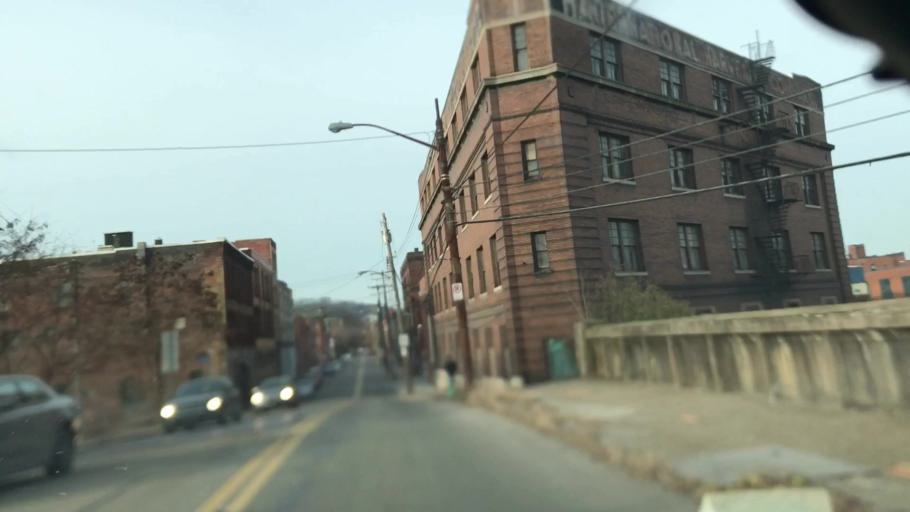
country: US
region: Pennsylvania
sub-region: Allegheny County
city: Pittsburgh
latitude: 40.4540
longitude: -80.0148
